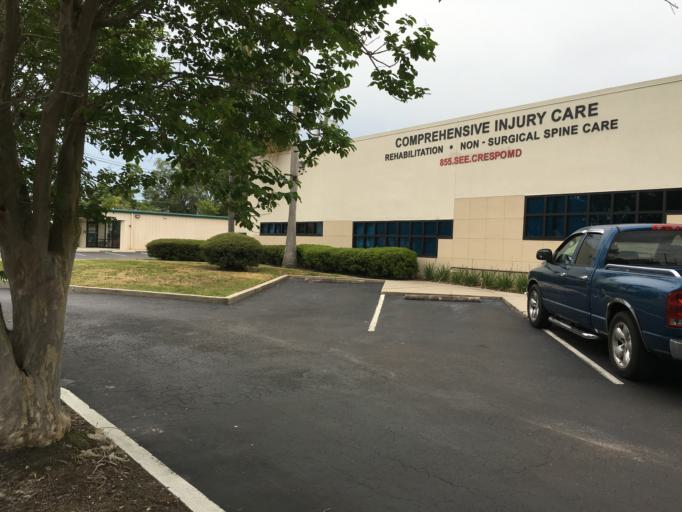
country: US
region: Florida
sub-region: Hillsborough County
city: Egypt Lake-Leto
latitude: 27.9525
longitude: -82.5294
